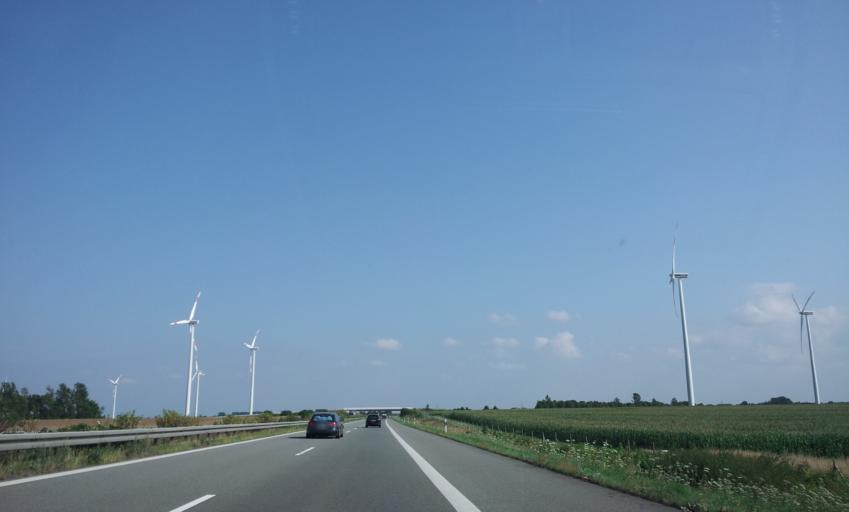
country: DE
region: Mecklenburg-Vorpommern
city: Dersekow
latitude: 54.0593
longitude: 13.2380
